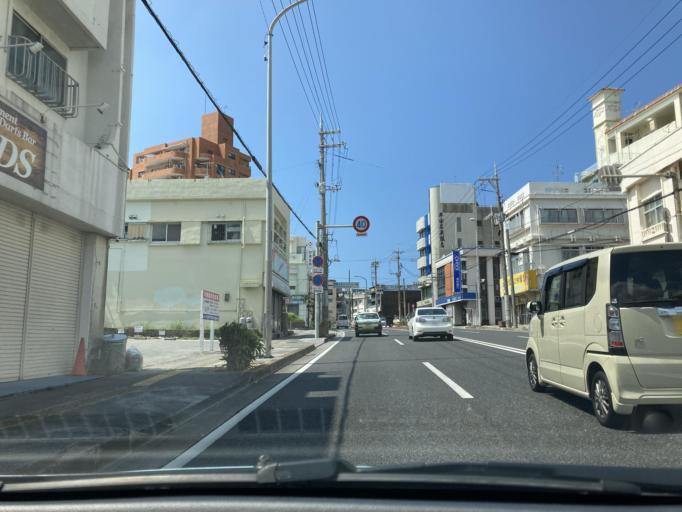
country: JP
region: Okinawa
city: Okinawa
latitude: 26.3376
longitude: 127.8032
